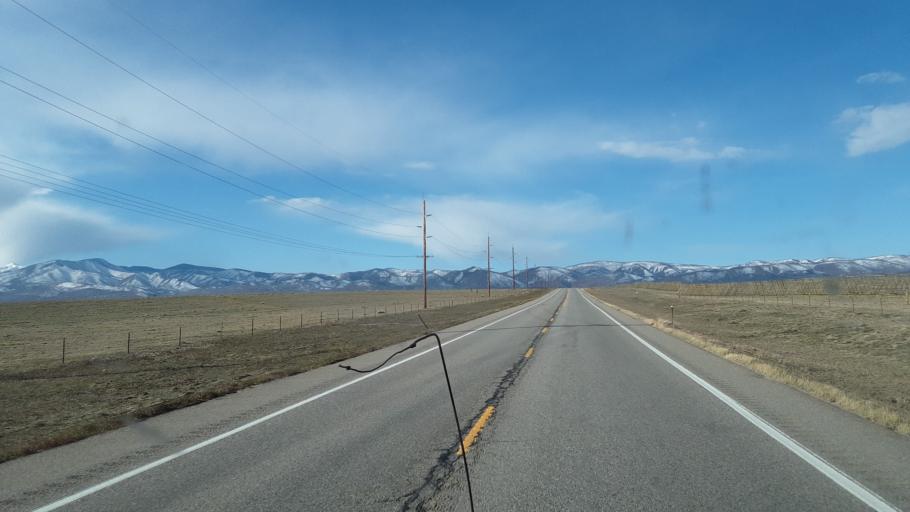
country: US
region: Colorado
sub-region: Huerfano County
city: Walsenburg
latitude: 37.5481
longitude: -104.9895
